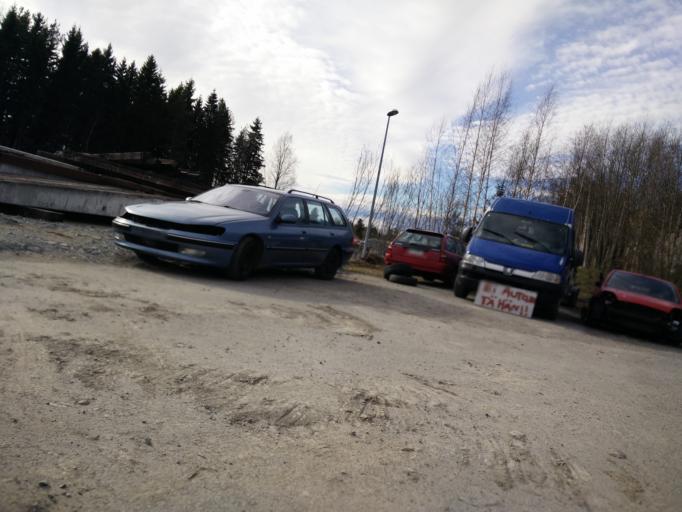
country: FI
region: Pirkanmaa
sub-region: Tampere
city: Orivesi
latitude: 61.6966
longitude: 24.3501
